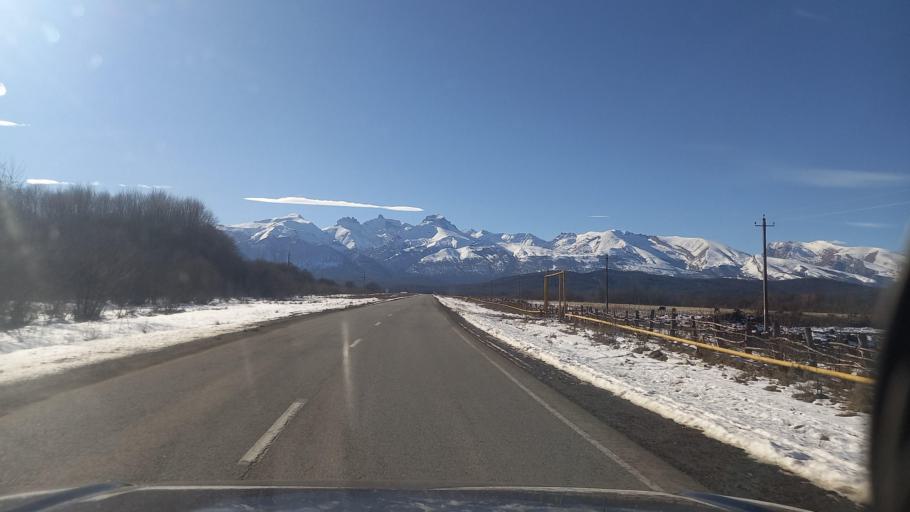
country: RU
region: North Ossetia
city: Chikola
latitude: 43.1484
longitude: 43.8361
